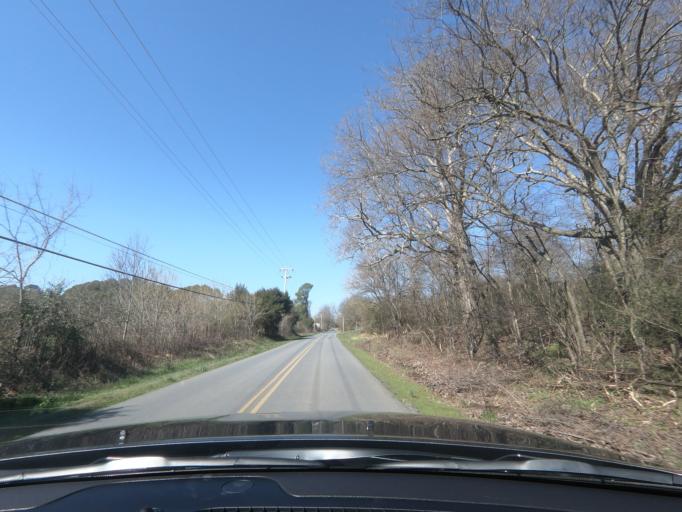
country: US
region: Georgia
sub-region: Bartow County
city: Rydal
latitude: 34.4442
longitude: -84.8086
